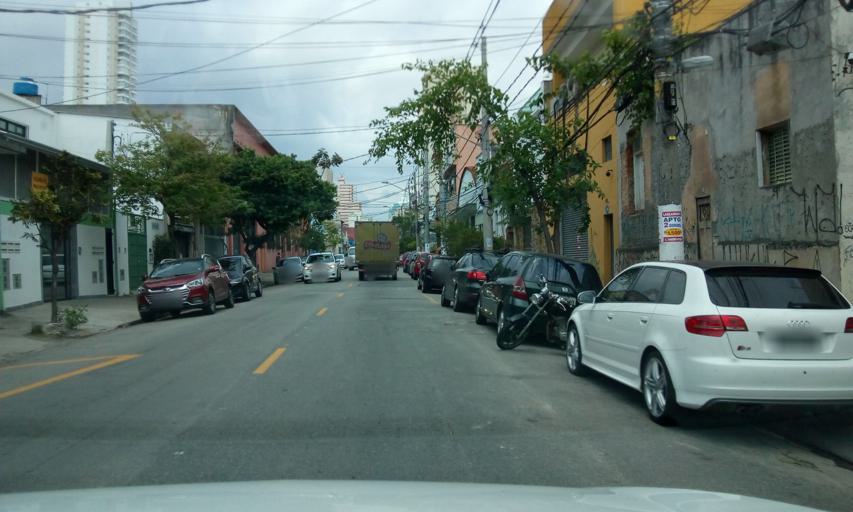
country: BR
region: Sao Paulo
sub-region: Sao Paulo
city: Sao Paulo
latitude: -23.5647
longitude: -46.6245
